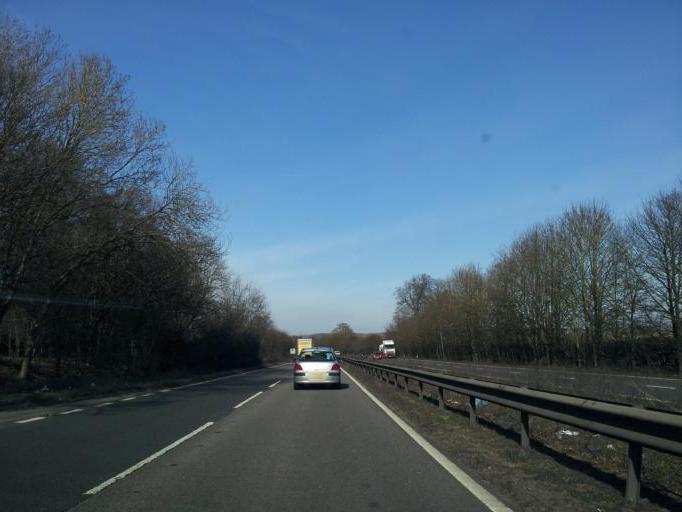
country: GB
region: England
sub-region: Lincolnshire
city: Grantham
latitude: 52.8479
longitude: -0.6276
